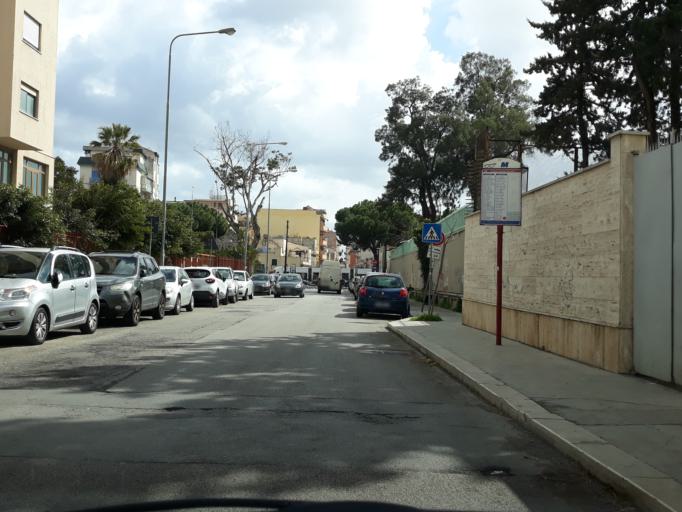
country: IT
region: Sicily
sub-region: Palermo
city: Palermo
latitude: 38.1227
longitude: 13.3277
